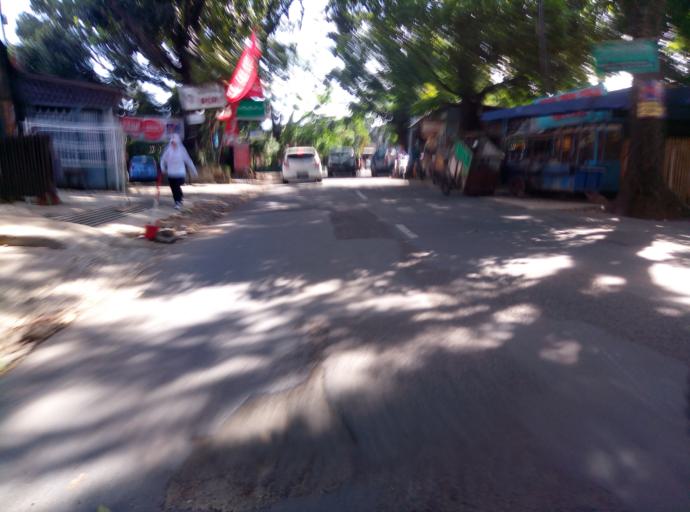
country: ID
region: West Java
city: Bandung
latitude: -6.8890
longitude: 107.6258
